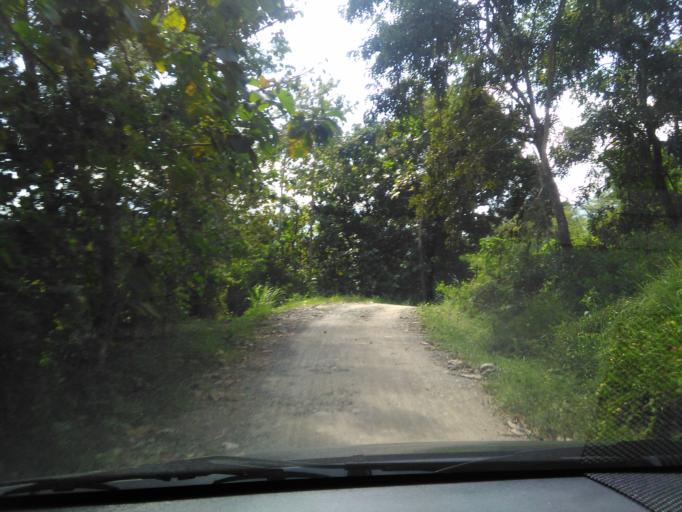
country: ID
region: South Sulawesi
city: Enrekang
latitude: -3.5152
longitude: 119.7336
